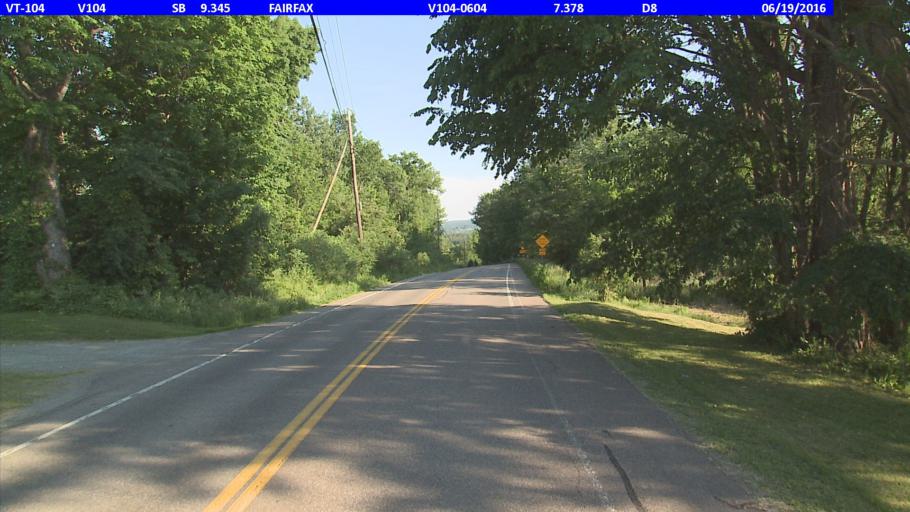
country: US
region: Vermont
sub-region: Chittenden County
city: Milton
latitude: 44.6913
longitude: -73.0334
